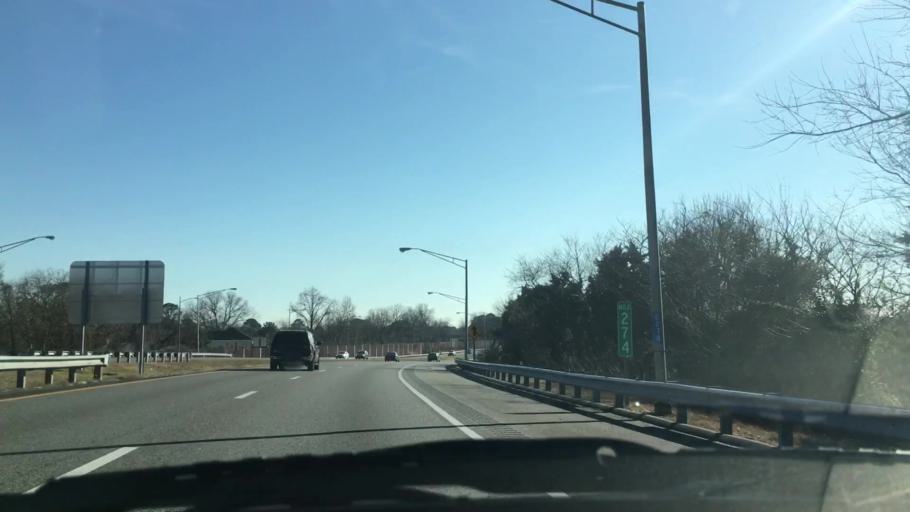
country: US
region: Virginia
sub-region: City of Hampton
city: East Hampton
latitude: 36.9568
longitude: -76.2637
